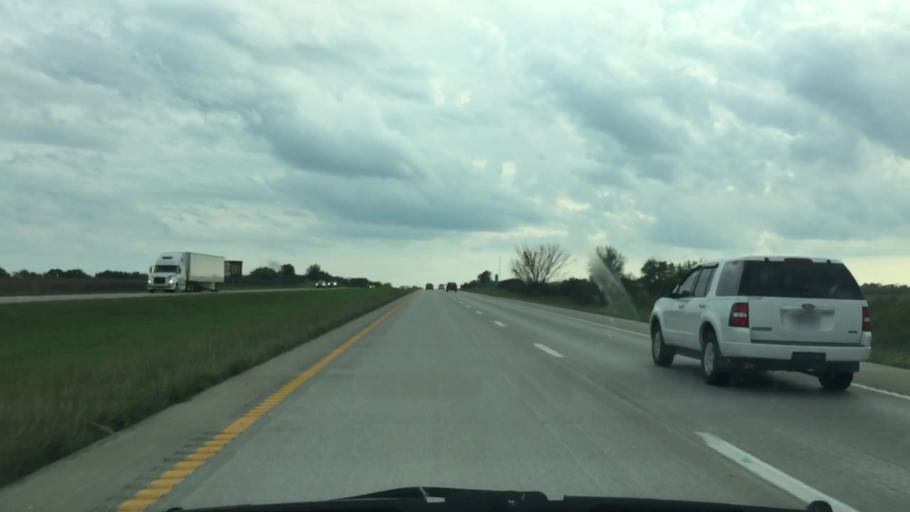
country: US
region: Missouri
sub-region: Clinton County
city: Cameron
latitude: 39.6315
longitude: -94.2455
